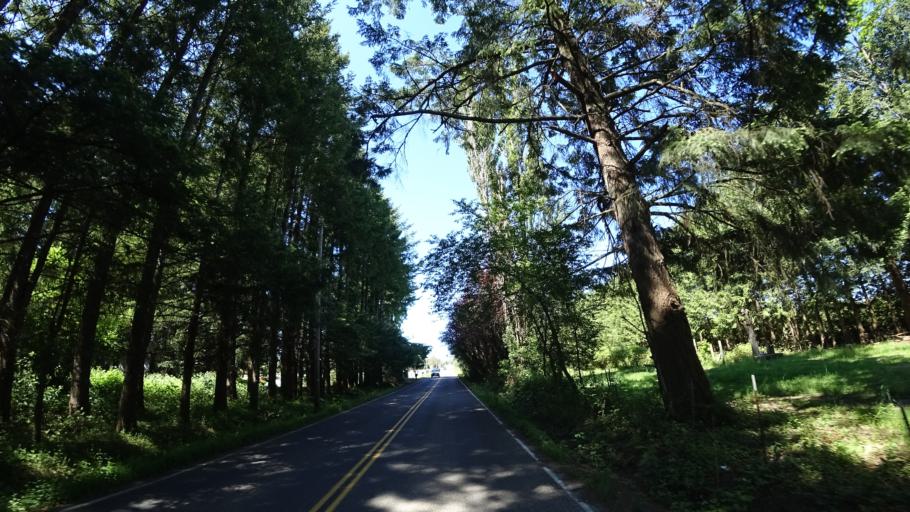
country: US
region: Oregon
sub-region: Multnomah County
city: Gresham
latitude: 45.4703
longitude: -122.4755
